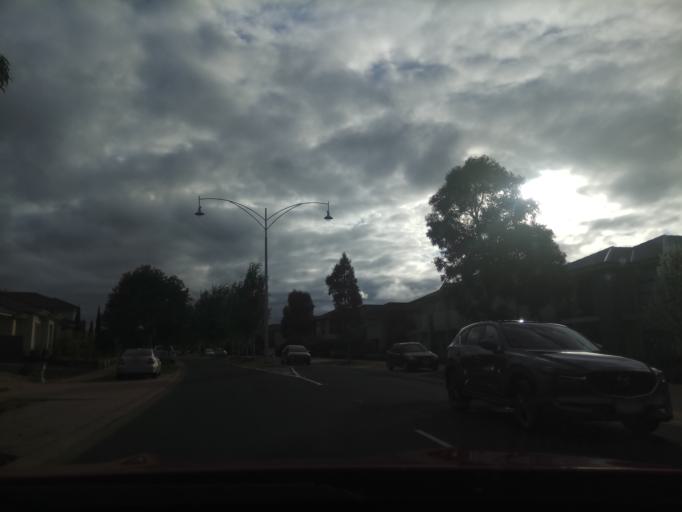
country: AU
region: Victoria
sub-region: Wyndham
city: Point Cook
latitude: -37.9028
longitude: 144.7699
